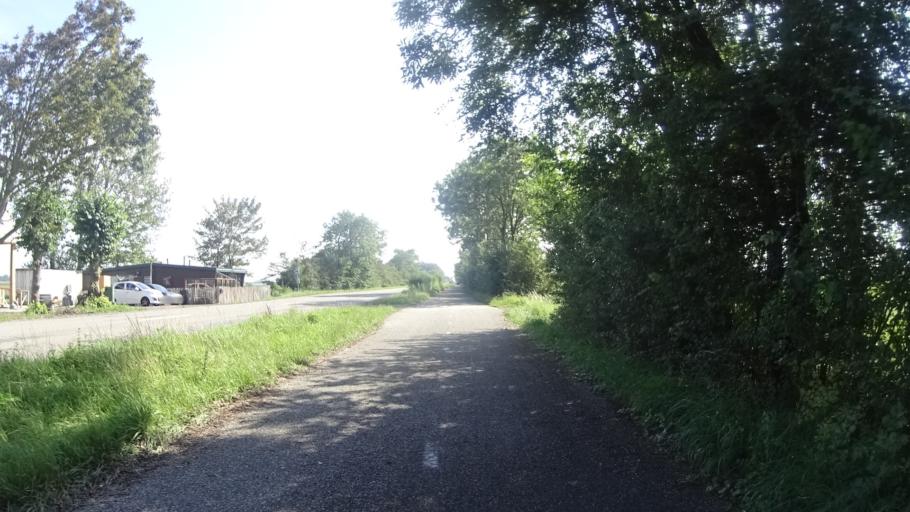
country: NL
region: Friesland
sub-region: Gemeente Franekeradeel
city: Tzum
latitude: 53.1912
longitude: 5.5836
